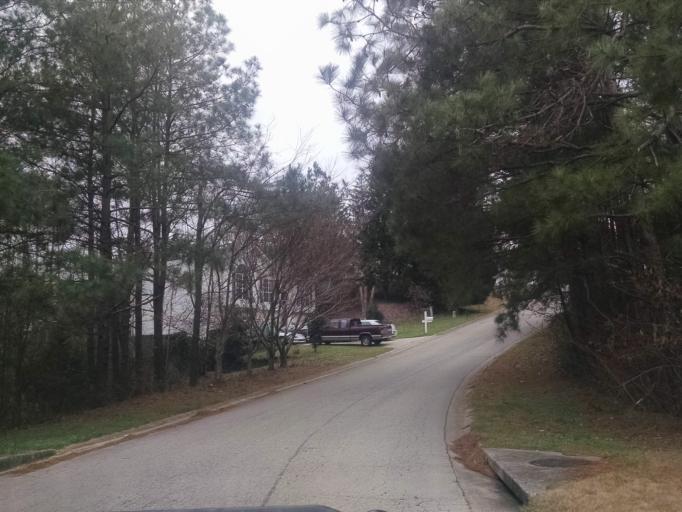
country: US
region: Georgia
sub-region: Hall County
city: Oakwood
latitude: 34.2029
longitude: -83.8635
